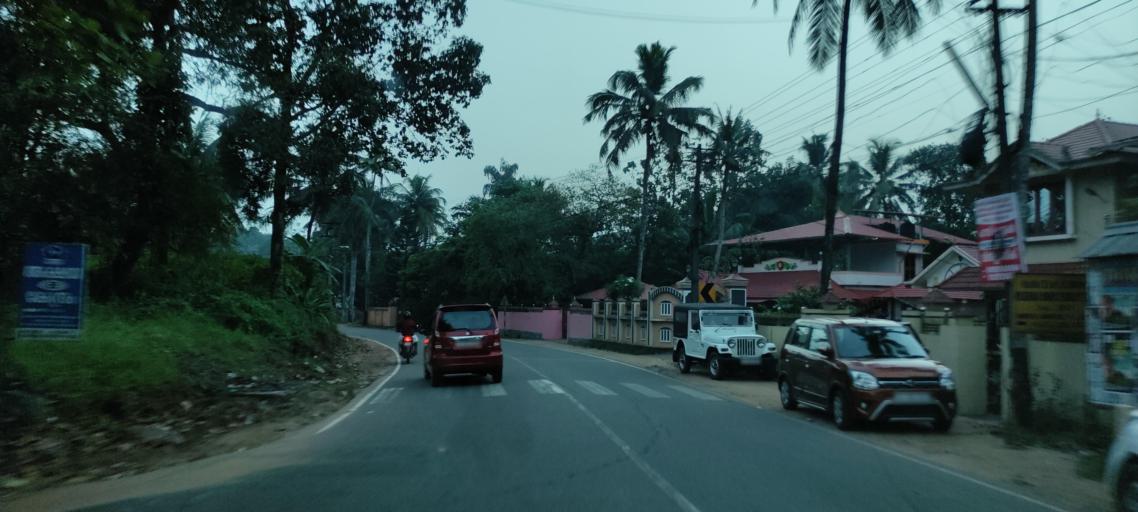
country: IN
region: Kerala
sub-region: Pattanamtitta
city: Adur
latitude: 9.1613
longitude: 76.7438
